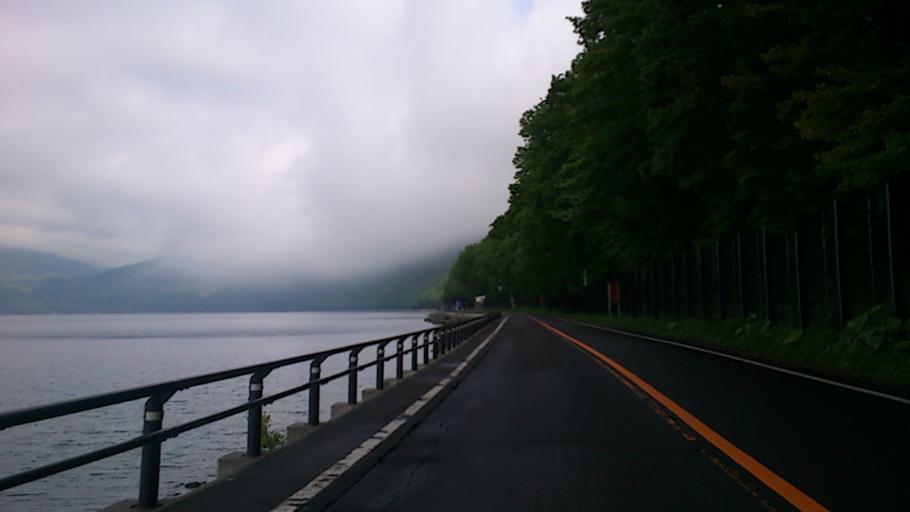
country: JP
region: Hokkaido
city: Shiraoi
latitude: 42.7886
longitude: 141.3758
